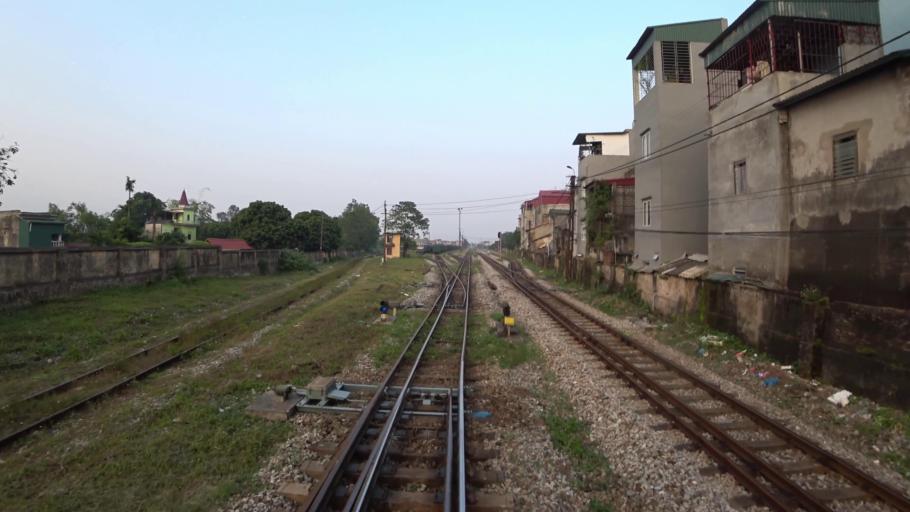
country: VN
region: Ha Noi
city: Dong Anh
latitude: 21.0955
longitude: 105.9114
